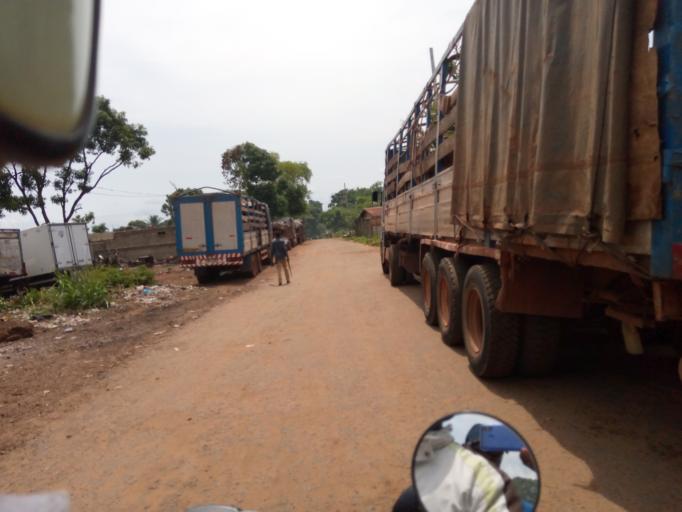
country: SL
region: Western Area
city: Waterloo
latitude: 8.3702
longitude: -13.0907
